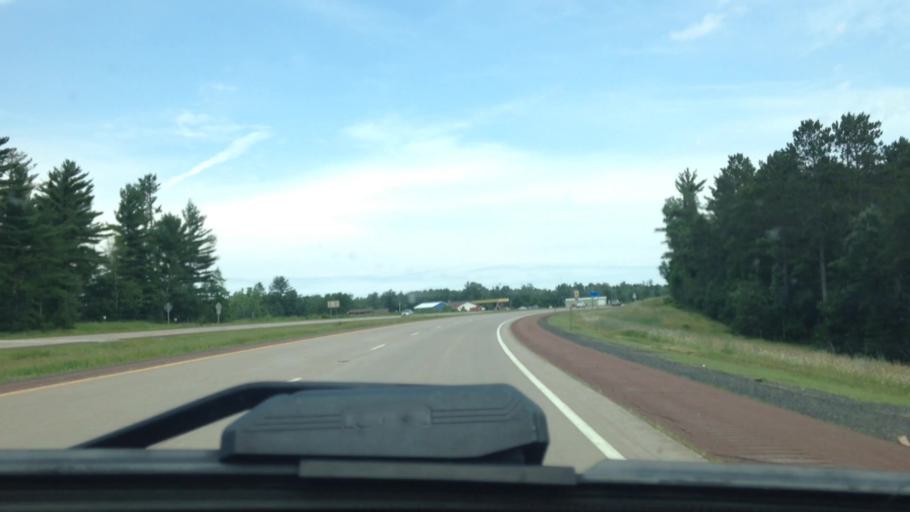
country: US
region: Wisconsin
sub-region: Douglas County
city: Lake Nebagamon
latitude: 46.3475
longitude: -91.8355
